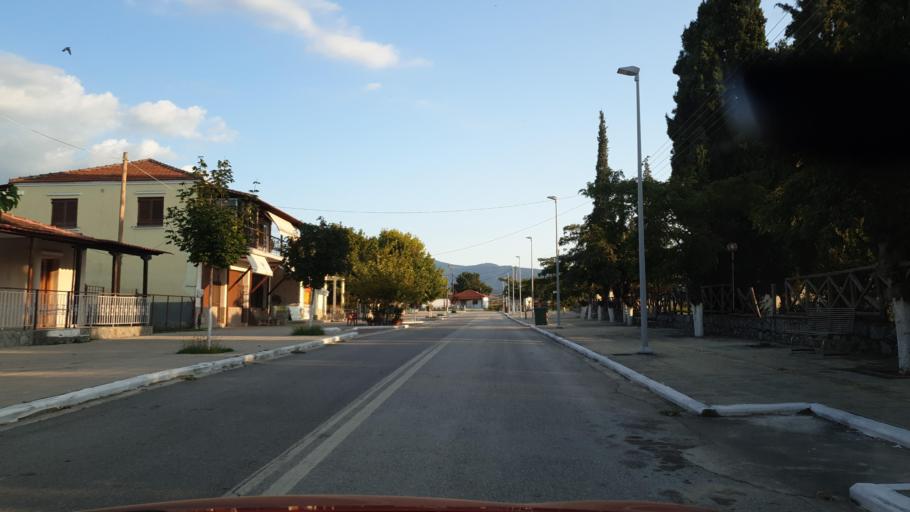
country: GR
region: Central Macedonia
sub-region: Nomos Thessalonikis
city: Nea Apollonia
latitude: 40.5588
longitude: 23.4727
